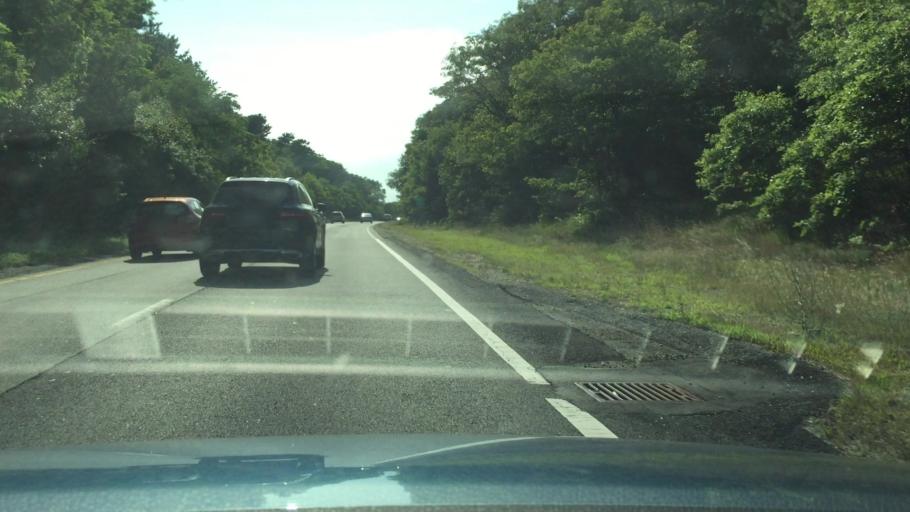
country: US
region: Massachusetts
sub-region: Barnstable County
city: West Barnstable
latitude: 41.6846
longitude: -70.3542
